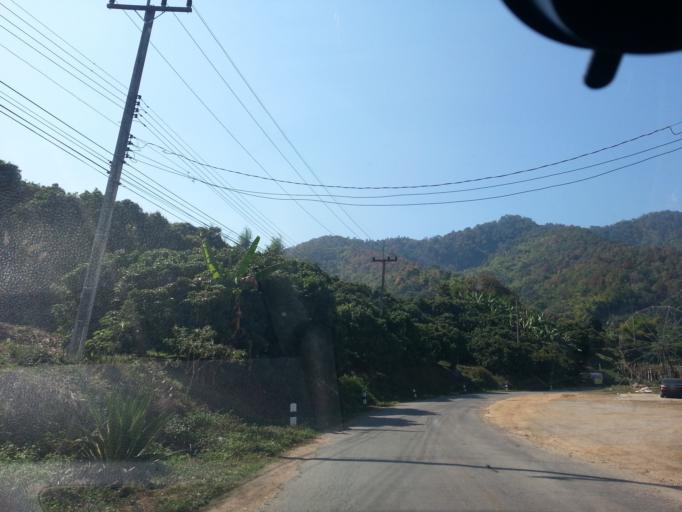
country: TH
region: Chiang Mai
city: Chai Prakan
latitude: 19.8170
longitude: 99.1018
